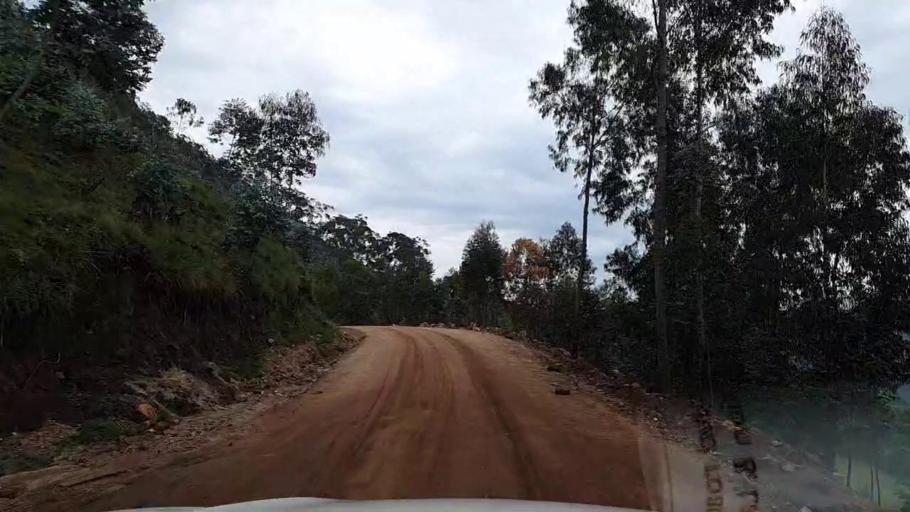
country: RW
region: Southern Province
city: Nzega
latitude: -2.3746
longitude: 29.4489
